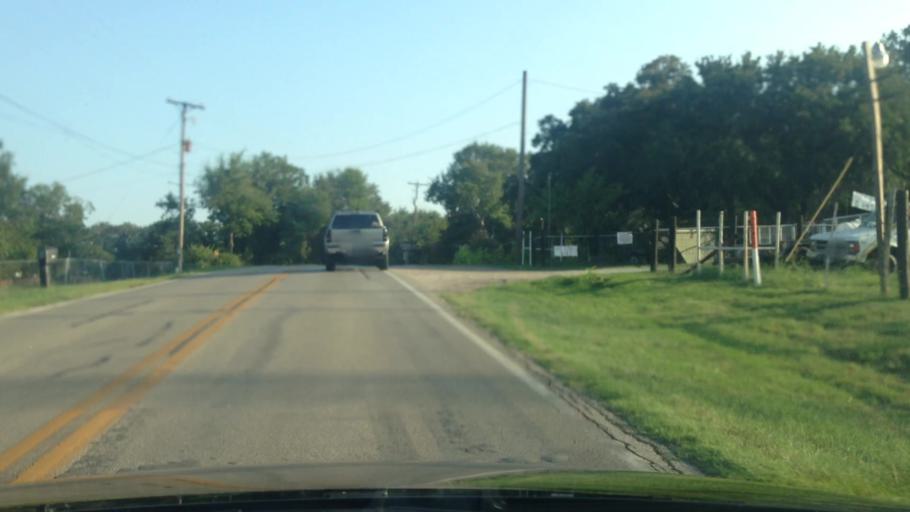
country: US
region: Texas
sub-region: Tarrant County
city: Rendon
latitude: 32.5944
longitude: -97.2589
